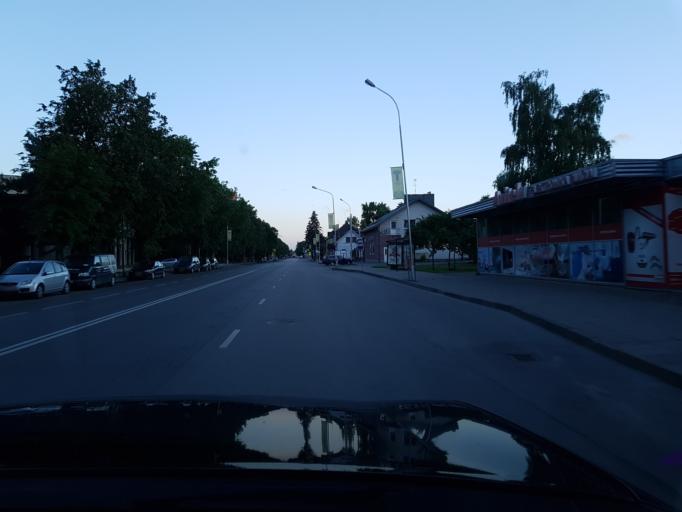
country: LT
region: Marijampoles apskritis
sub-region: Marijampole Municipality
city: Marijampole
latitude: 54.5665
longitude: 23.3585
